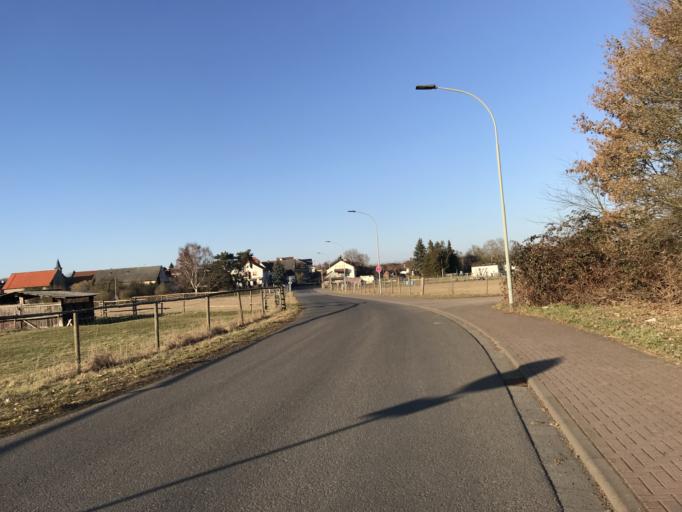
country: DE
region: Hesse
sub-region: Regierungsbezirk Giessen
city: Hungen
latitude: 50.4544
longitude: 8.8984
